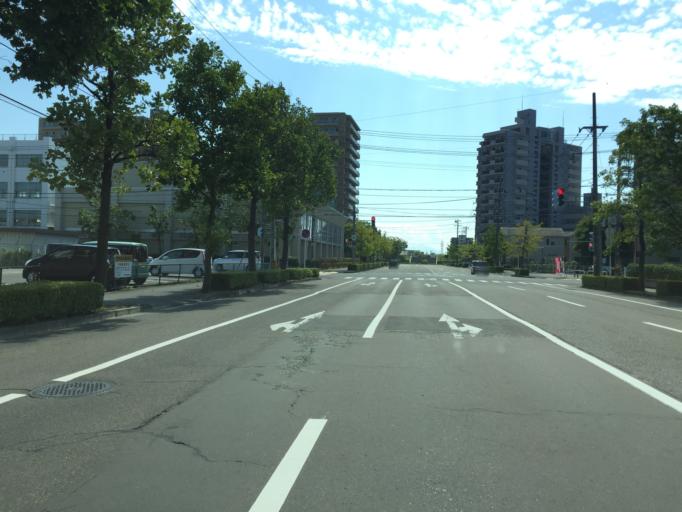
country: JP
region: Niigata
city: Niigata-shi
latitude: 37.9112
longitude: 139.0318
